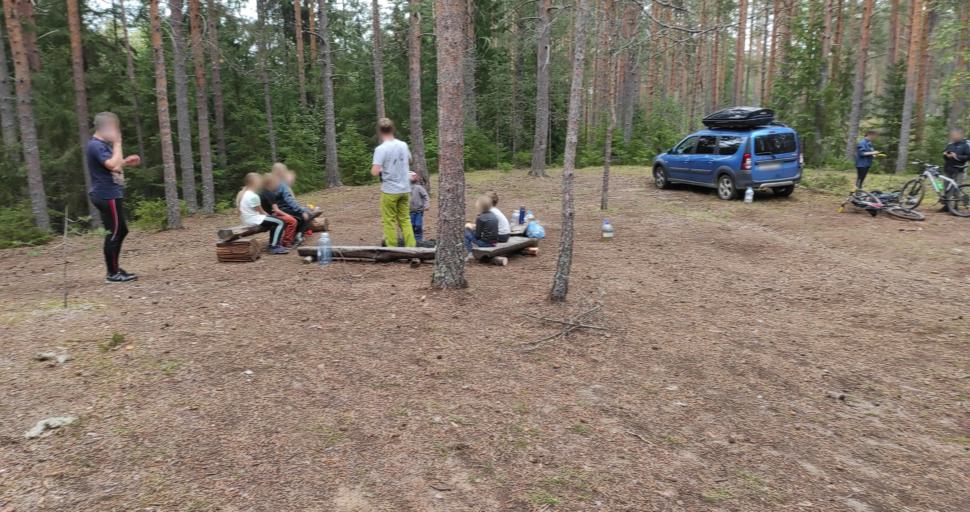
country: RU
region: Leningrad
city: Sosnovo
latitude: 60.6066
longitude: 30.1022
